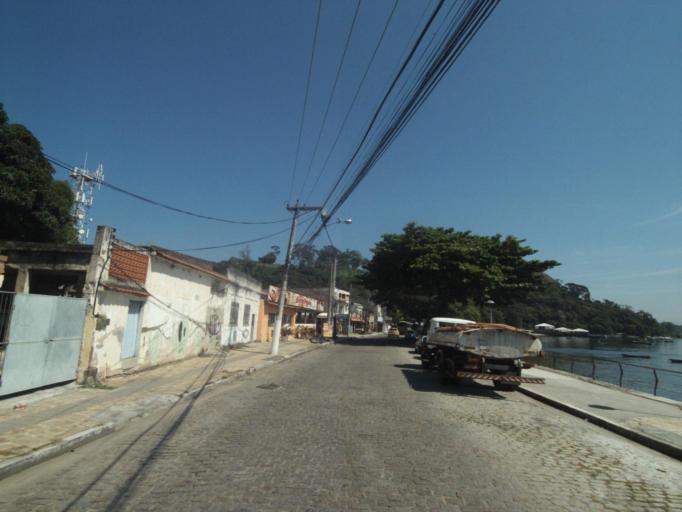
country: BR
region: Rio de Janeiro
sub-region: Niteroi
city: Niteroi
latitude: -22.9277
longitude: -43.1183
